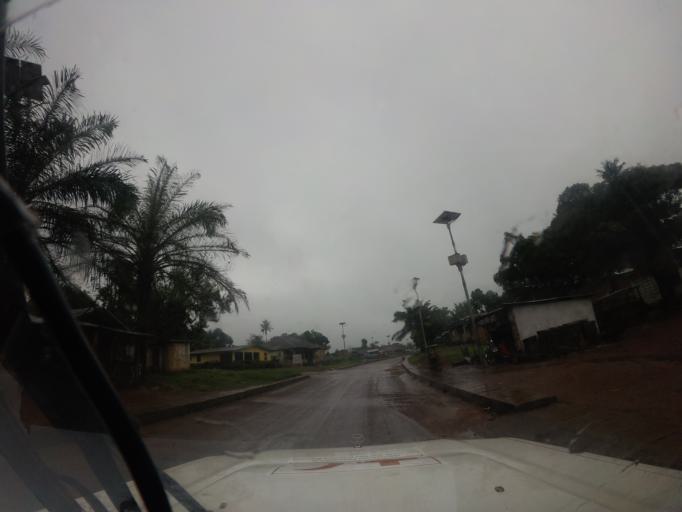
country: SL
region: Northern Province
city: Binkolo
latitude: 8.9541
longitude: -11.9777
